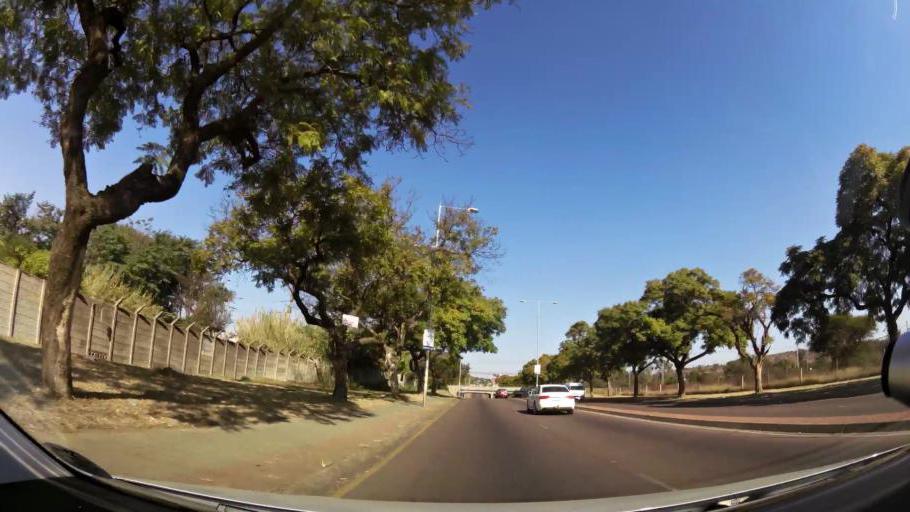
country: ZA
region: Gauteng
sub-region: City of Tshwane Metropolitan Municipality
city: Pretoria
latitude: -25.7202
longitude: 28.1865
